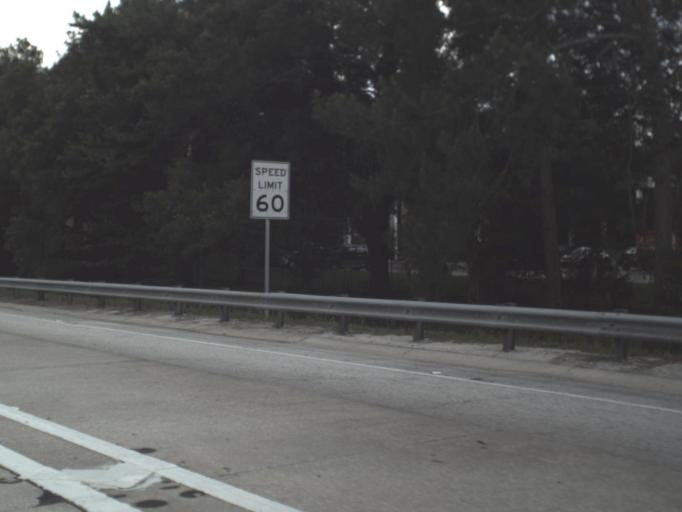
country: US
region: Florida
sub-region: Duval County
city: Jacksonville
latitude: 30.3060
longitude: -81.6167
